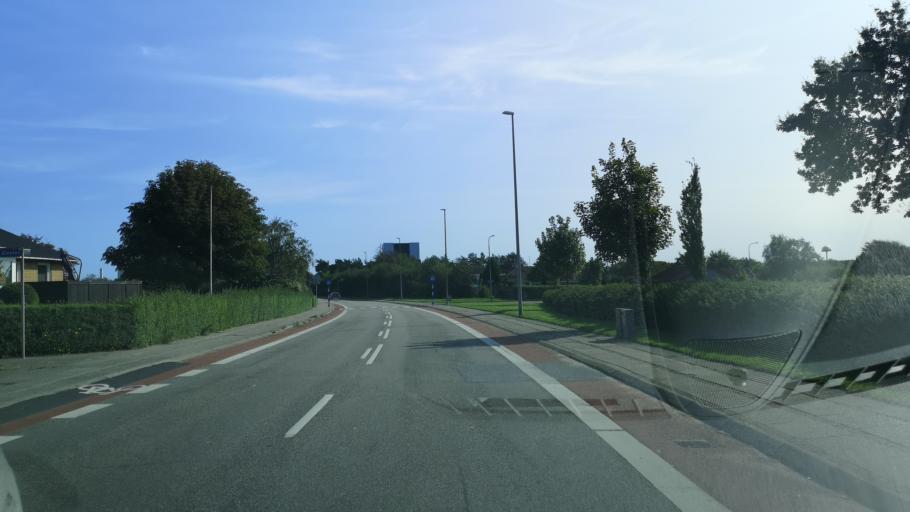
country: DK
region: Central Jutland
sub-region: Ringkobing-Skjern Kommune
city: Videbaek
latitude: 56.0857
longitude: 8.6218
